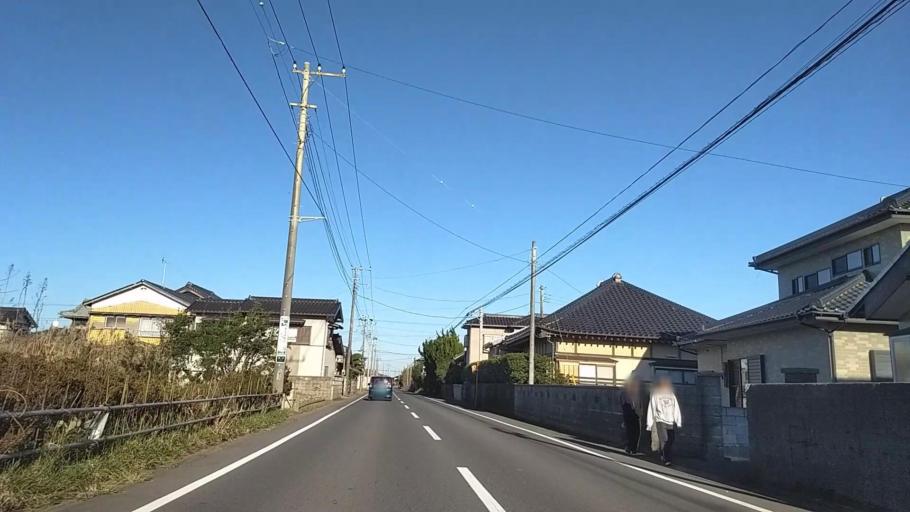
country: JP
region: Chiba
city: Yokaichiba
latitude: 35.6607
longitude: 140.5996
